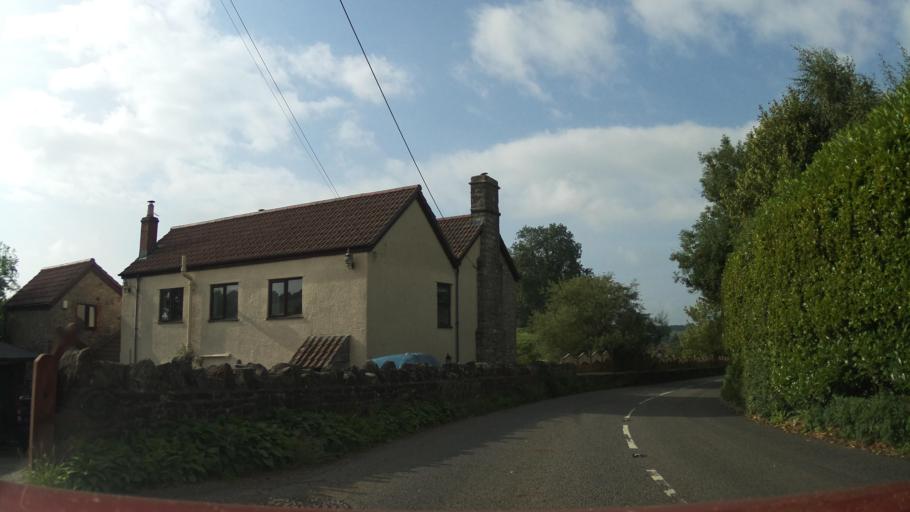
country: GB
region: England
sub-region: North Somerset
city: Winford
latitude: 51.3895
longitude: -2.6632
